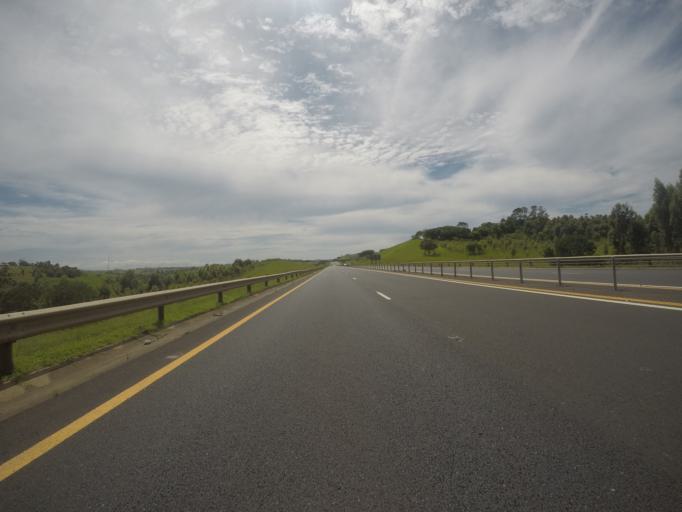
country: ZA
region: KwaZulu-Natal
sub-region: iLembe District Municipality
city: Mandeni
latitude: -29.1801
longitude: 31.4965
